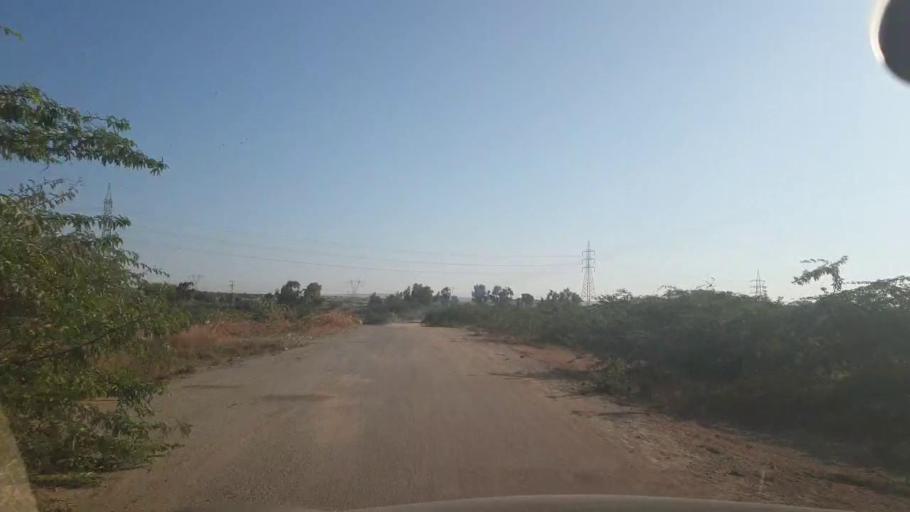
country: PK
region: Sindh
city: Malir Cantonment
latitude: 25.1190
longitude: 67.2826
